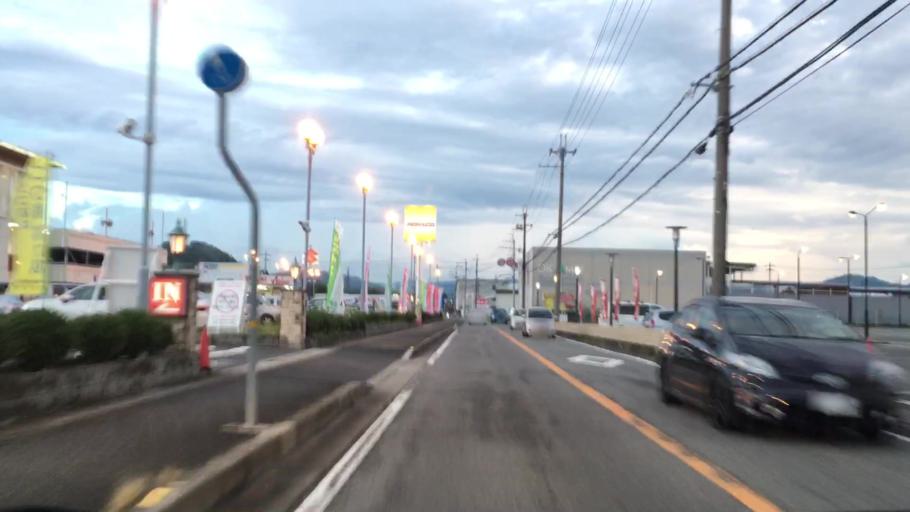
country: JP
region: Hyogo
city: Himeji
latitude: 34.9215
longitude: 134.7432
